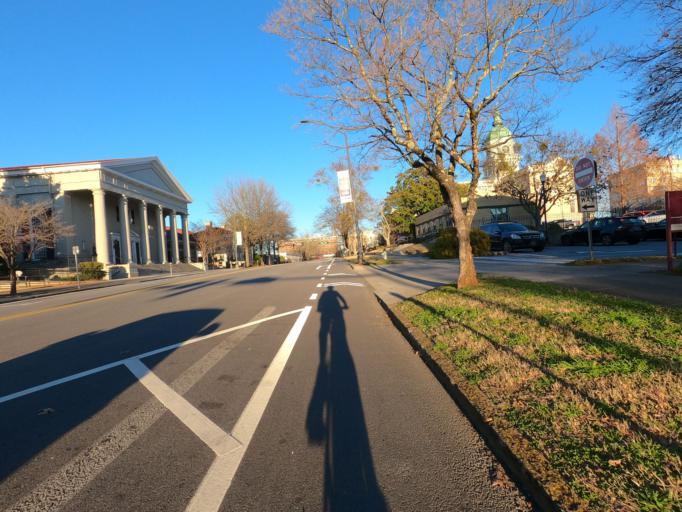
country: US
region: Georgia
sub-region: Clarke County
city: Athens
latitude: 33.9599
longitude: -83.3773
